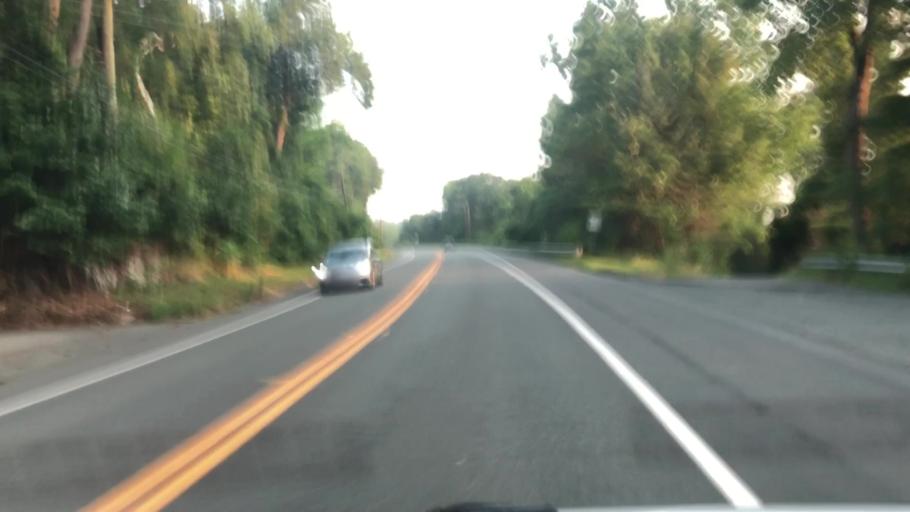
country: US
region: Massachusetts
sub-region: Franklin County
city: Greenfield
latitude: 42.5925
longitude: -72.6319
